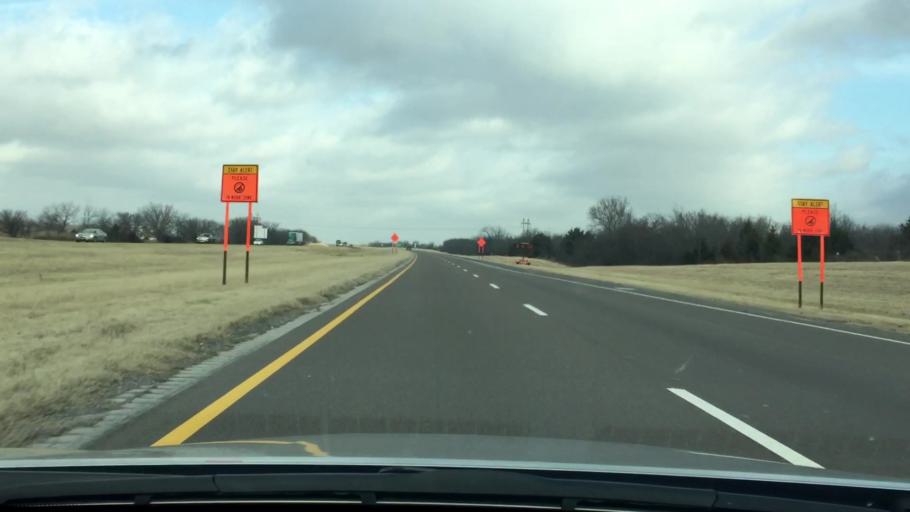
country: US
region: Oklahoma
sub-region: Garvin County
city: Maysville
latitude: 34.8307
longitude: -97.3106
